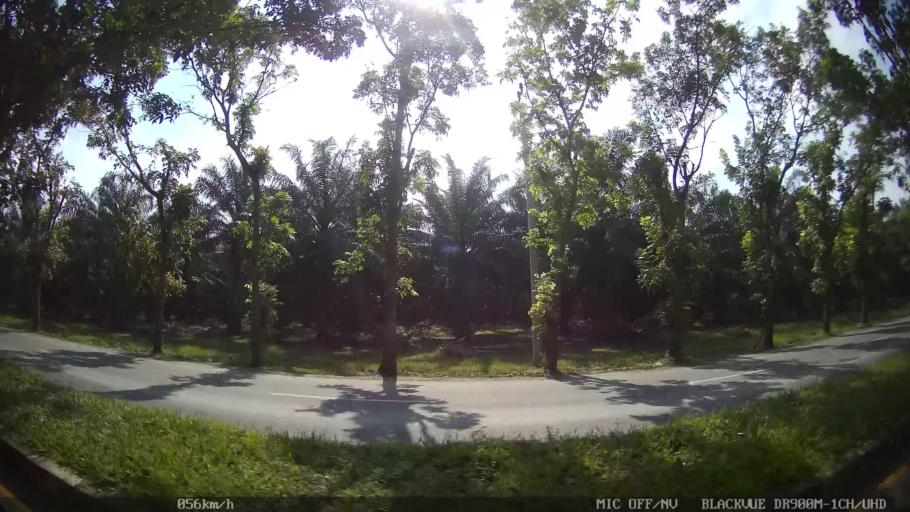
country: ID
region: North Sumatra
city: Binjai
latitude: 3.6433
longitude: 98.5354
